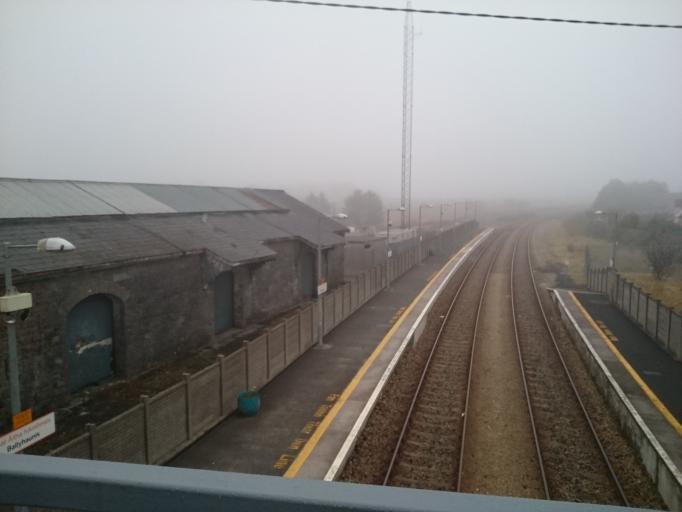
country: IE
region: Connaught
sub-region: Maigh Eo
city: Ballyhaunis
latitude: 53.7616
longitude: -8.7583
